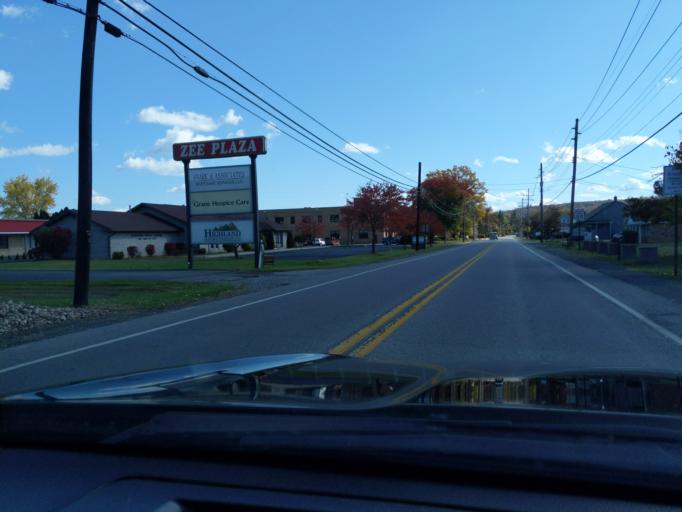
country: US
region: Pennsylvania
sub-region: Blair County
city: Hollidaysburg
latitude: 40.4363
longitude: -78.4095
